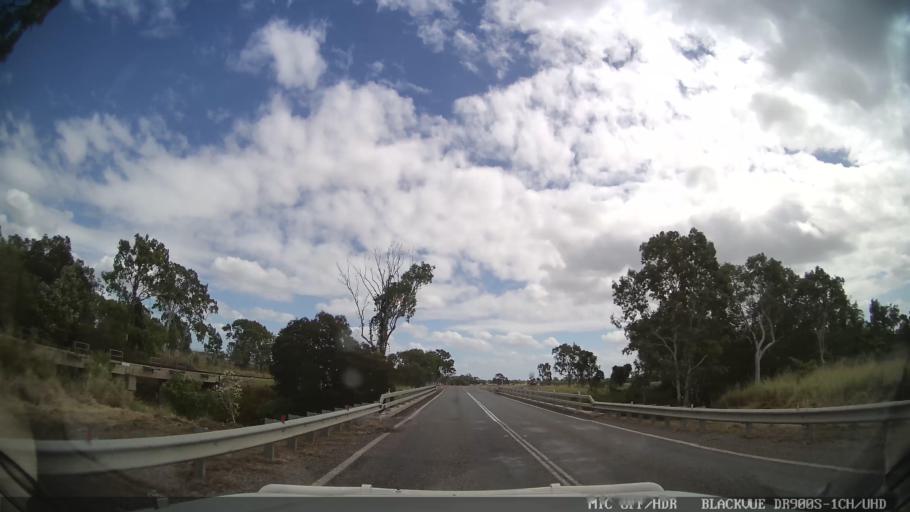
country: AU
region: Queensland
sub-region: Burdekin
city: Home Hill
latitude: -19.9082
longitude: 147.7781
